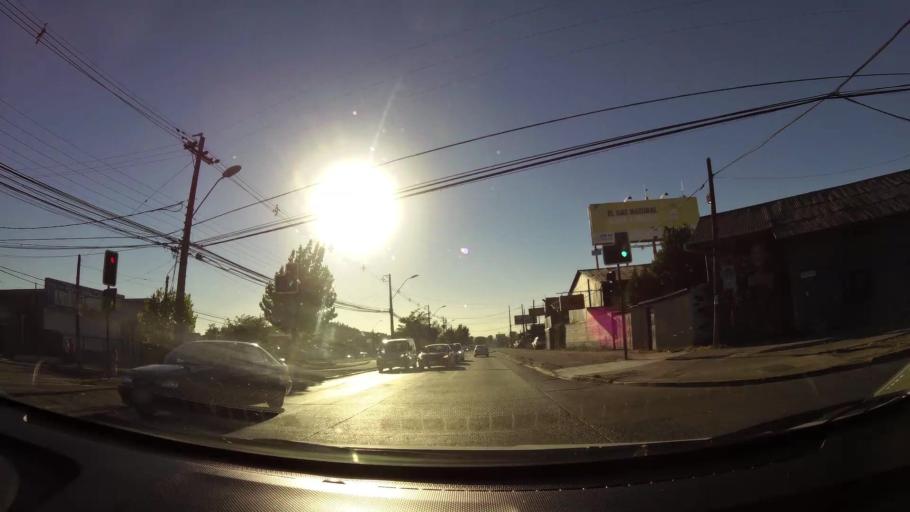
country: CL
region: Maule
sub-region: Provincia de Curico
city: Curico
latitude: -34.9764
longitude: -71.2135
